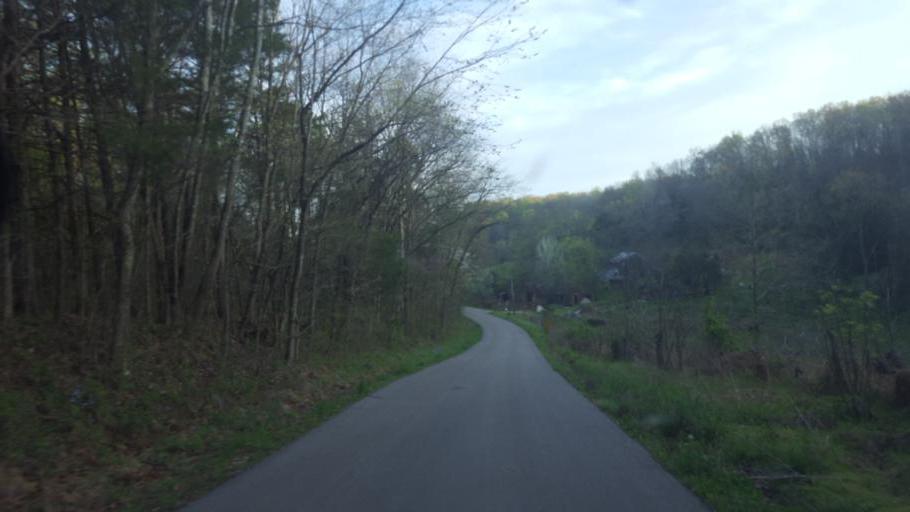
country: US
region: Kentucky
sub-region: Barren County
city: Cave City
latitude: 37.1750
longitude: -86.0017
